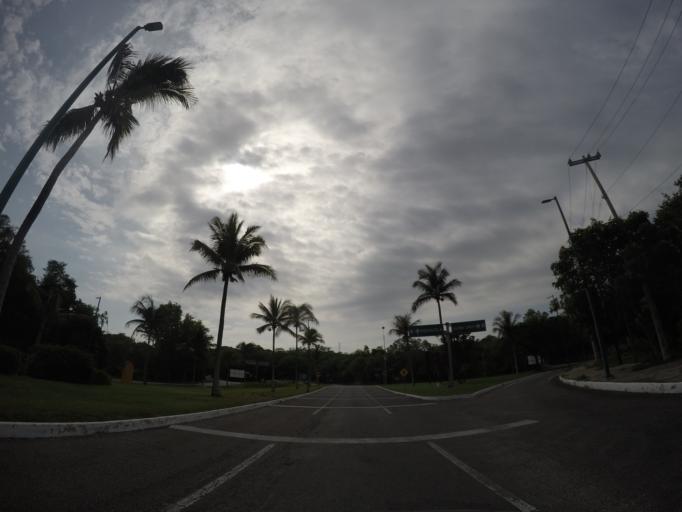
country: MX
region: Oaxaca
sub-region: Santa Maria Huatulco
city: Sector H Tres
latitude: 15.7819
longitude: -96.1564
